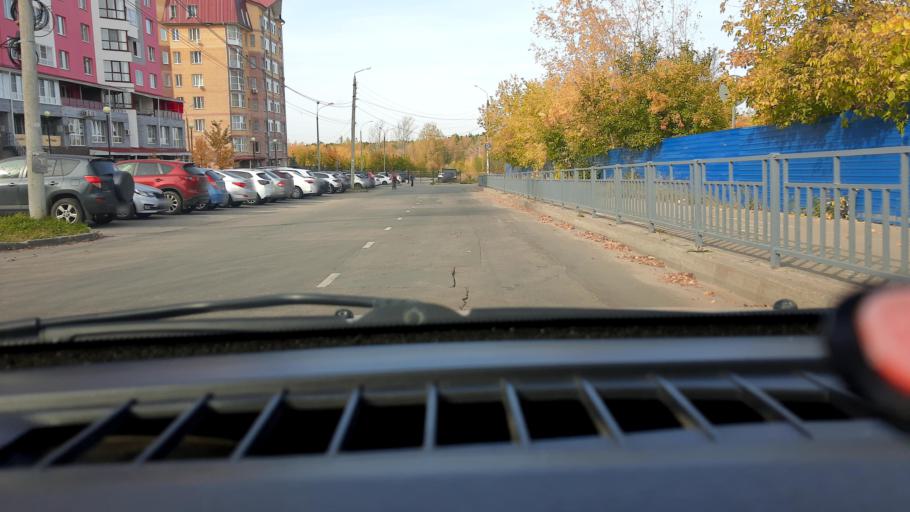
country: RU
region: Nizjnij Novgorod
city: Kstovo
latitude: 56.1527
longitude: 44.1857
